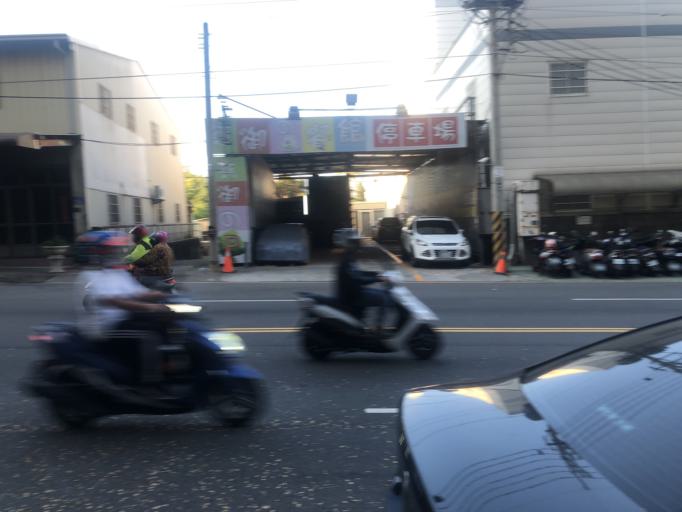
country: TW
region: Taiwan
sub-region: Taichung City
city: Taichung
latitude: 24.1383
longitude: 120.6080
